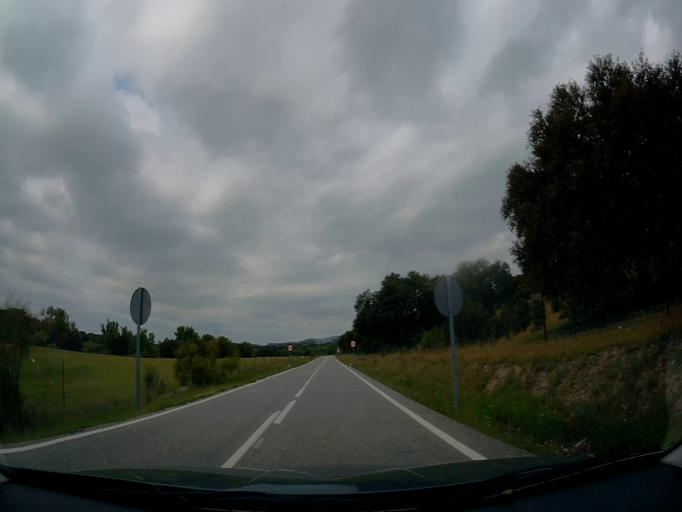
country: ES
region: Madrid
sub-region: Provincia de Madrid
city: Quijorna
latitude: 40.4202
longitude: -4.0860
